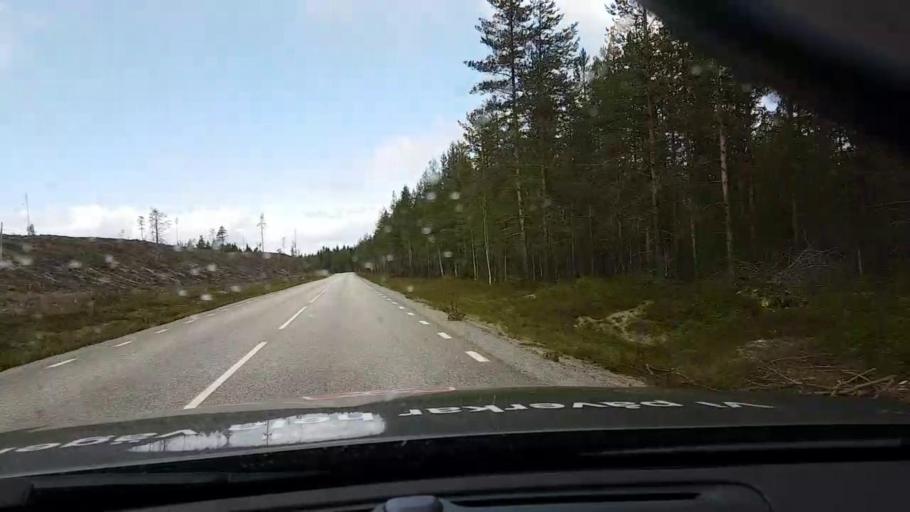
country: SE
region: Vaesternorrland
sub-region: OErnskoeldsviks Kommun
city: Bredbyn
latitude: 63.7063
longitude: 17.7599
